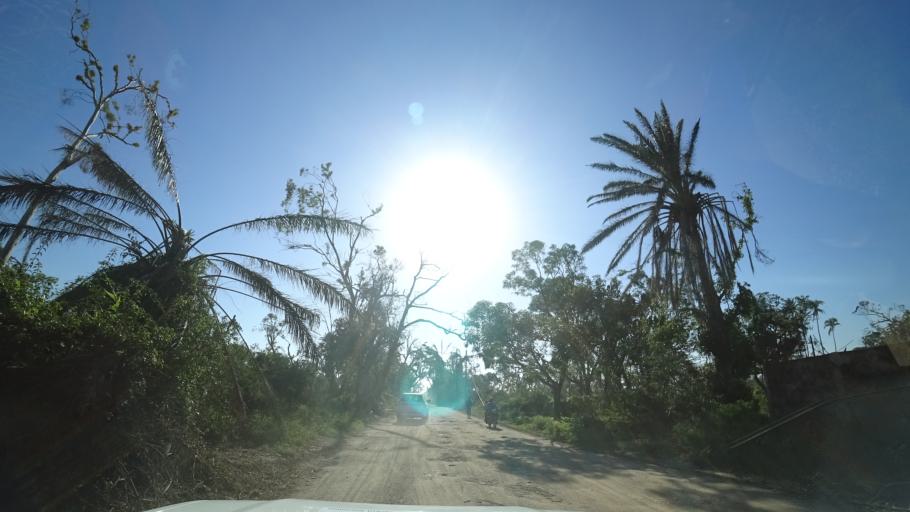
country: MZ
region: Sofala
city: Beira
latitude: -19.7659
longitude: 34.8952
